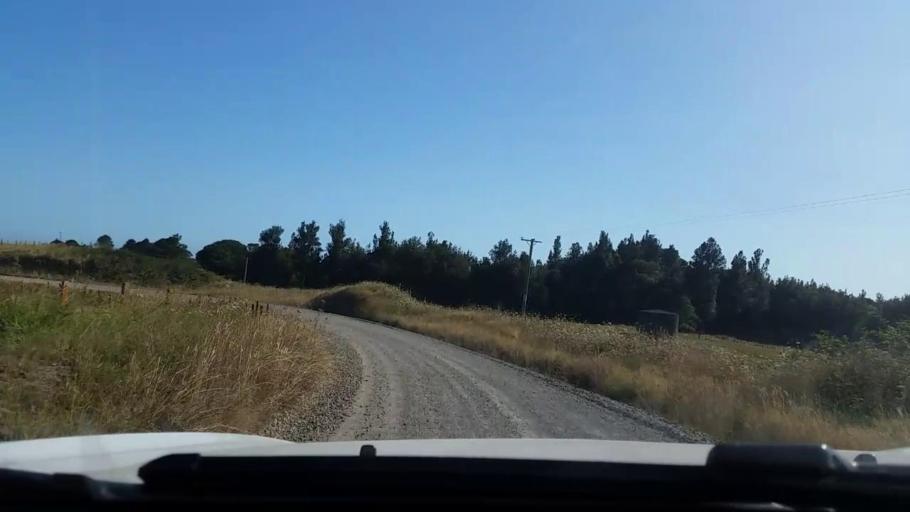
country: NZ
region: Bay of Plenty
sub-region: Western Bay of Plenty District
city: Maketu
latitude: -37.9692
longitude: 176.4360
